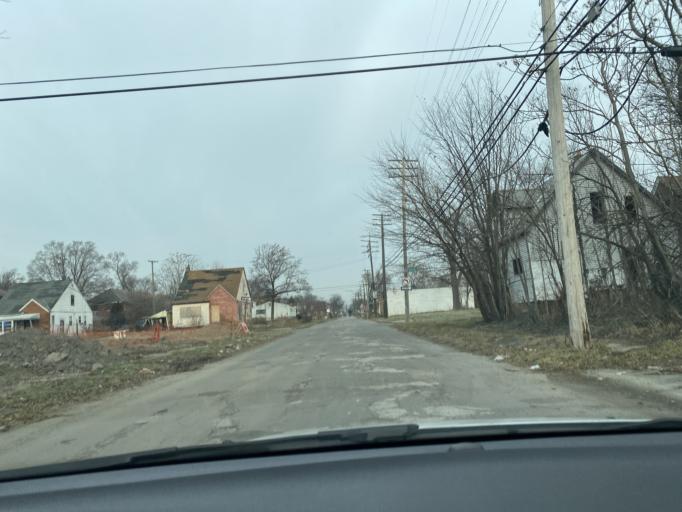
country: US
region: Michigan
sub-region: Wayne County
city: Highland Park
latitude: 42.3783
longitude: -83.1287
